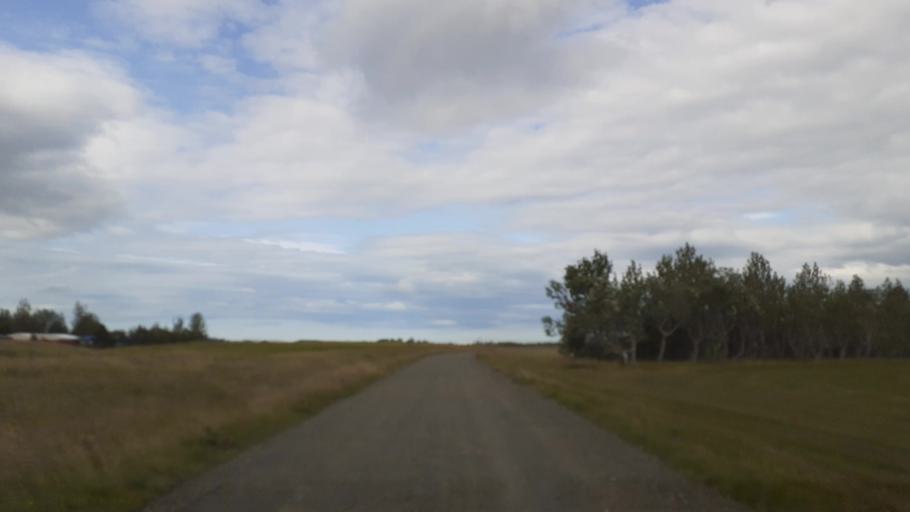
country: IS
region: South
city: Vestmannaeyjar
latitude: 63.7564
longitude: -20.2196
